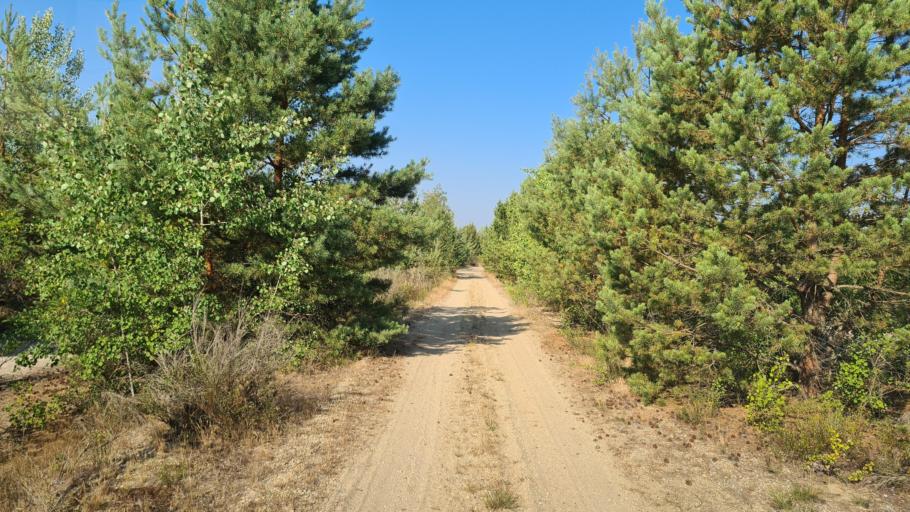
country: DE
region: Brandenburg
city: Sallgast
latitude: 51.5662
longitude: 13.8229
